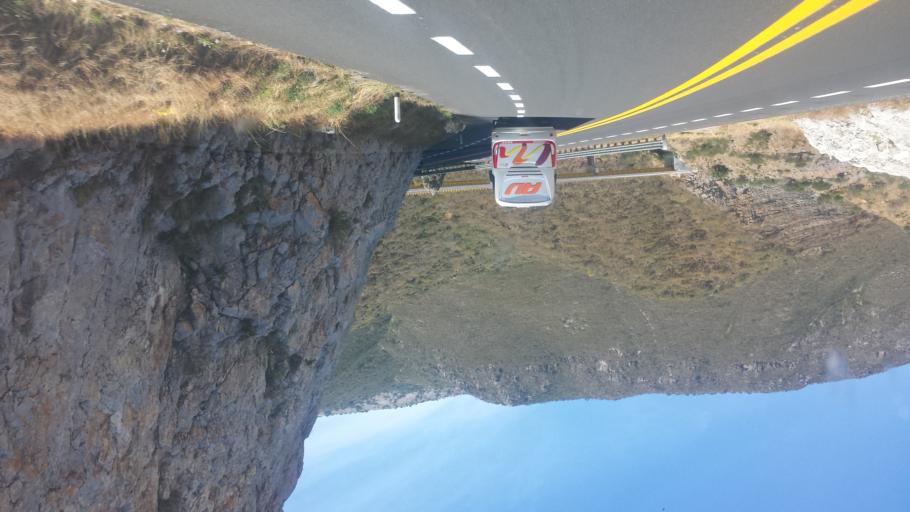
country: MX
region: Puebla
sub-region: San Jose Miahuatlan
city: San Pedro Tetitlan
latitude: 18.0906
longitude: -97.3437
